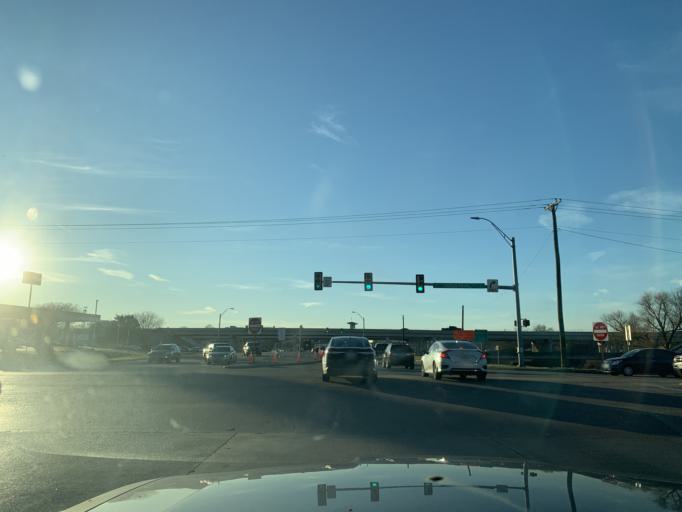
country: US
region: Texas
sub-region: Tarrant County
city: Euless
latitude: 32.8663
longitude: -97.0996
